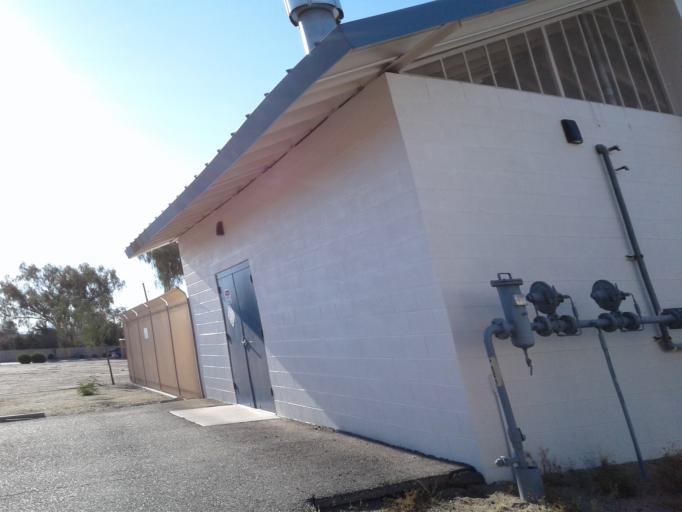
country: US
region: Arizona
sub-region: Maricopa County
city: Paradise Valley
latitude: 33.6477
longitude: -111.9973
